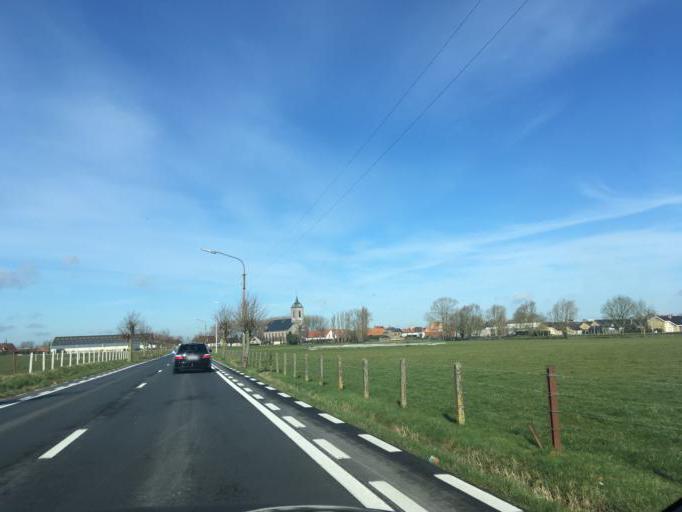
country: BE
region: Flanders
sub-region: Provincie West-Vlaanderen
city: Ledegem
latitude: 50.8510
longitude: 3.1330
